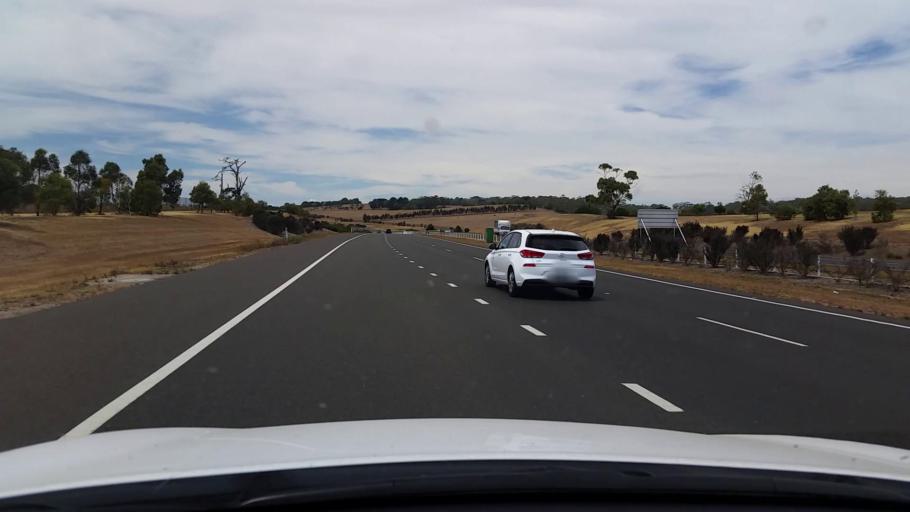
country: AU
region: Victoria
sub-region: Mornington Peninsula
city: Mount Martha
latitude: -38.2701
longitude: 145.0755
